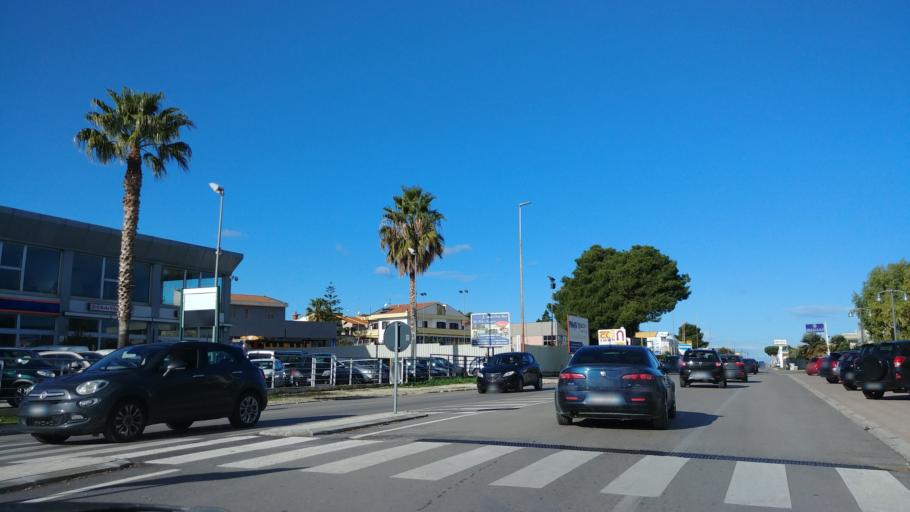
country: IT
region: Molise
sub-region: Provincia di Campobasso
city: Termoli
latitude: 41.9826
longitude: 15.0059
